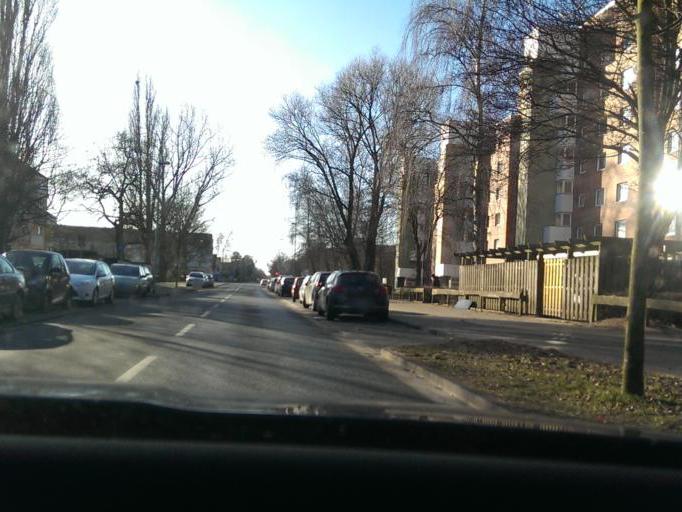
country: DE
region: Lower Saxony
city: Langenhagen
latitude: 52.4172
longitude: 9.7816
